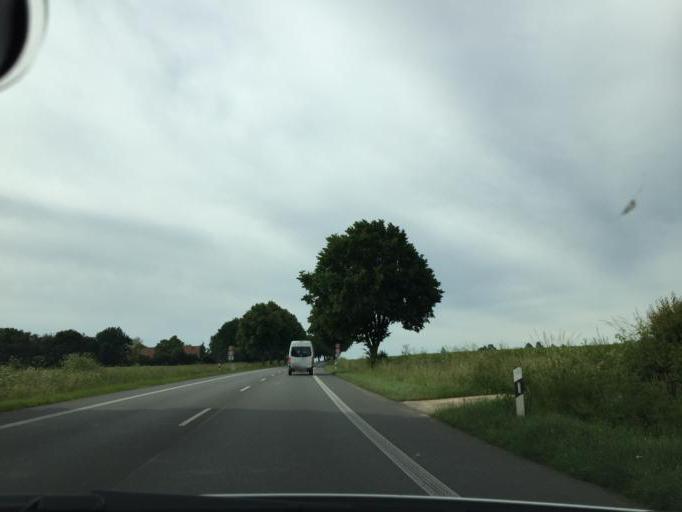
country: DE
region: North Rhine-Westphalia
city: Warburg
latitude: 51.5423
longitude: 9.1335
